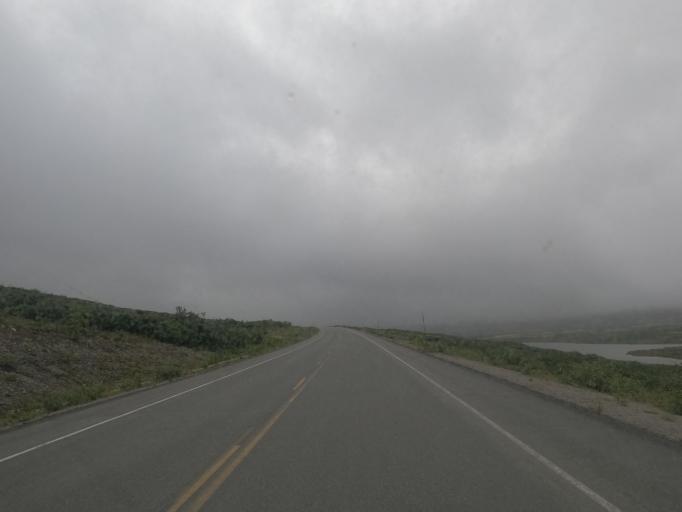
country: US
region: Alaska
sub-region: Haines Borough
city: Haines
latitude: 59.6899
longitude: -136.5839
